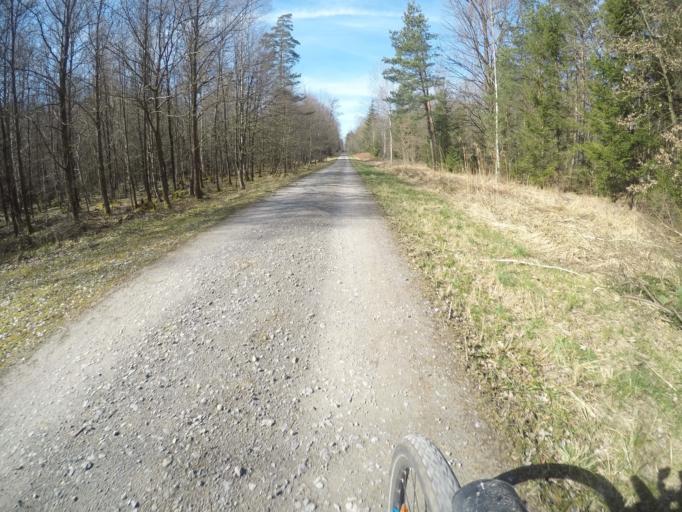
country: DE
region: Baden-Wuerttemberg
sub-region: Regierungsbezirk Stuttgart
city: Gerlingen
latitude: 48.7654
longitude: 9.0766
